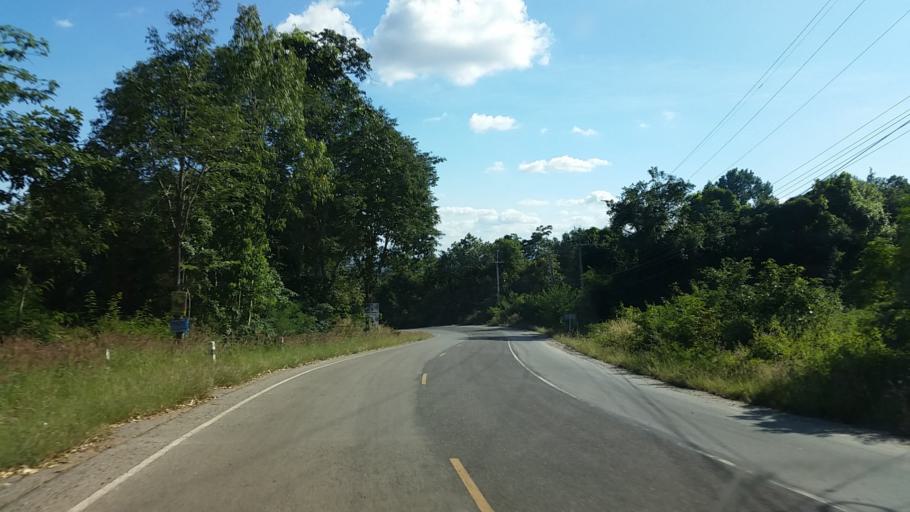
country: TH
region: Chaiyaphum
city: Thep Sathit
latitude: 15.5402
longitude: 101.4157
